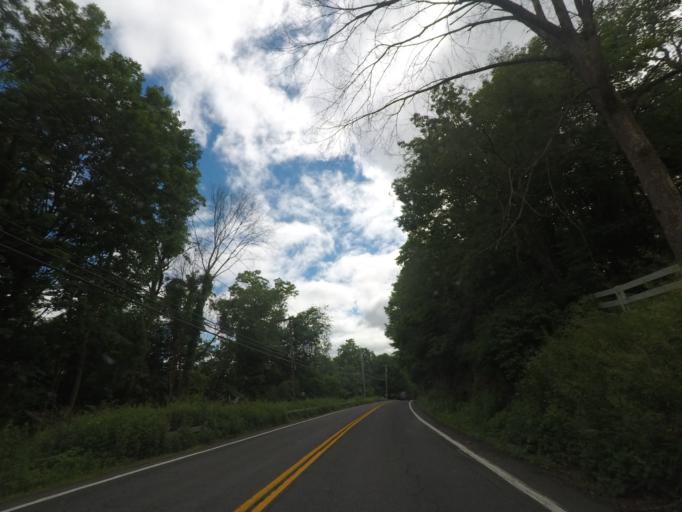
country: US
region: New York
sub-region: Columbia County
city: Philmont
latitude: 42.2475
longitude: -73.6750
